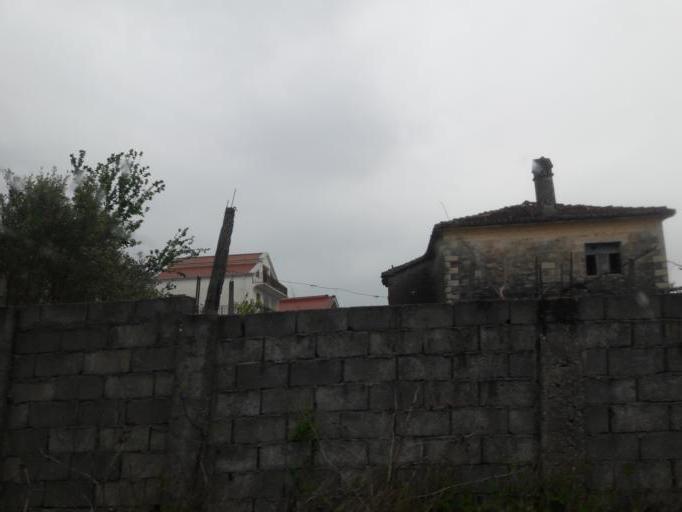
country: AL
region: Shkoder
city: Vukatane
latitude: 42.0107
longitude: 19.5339
